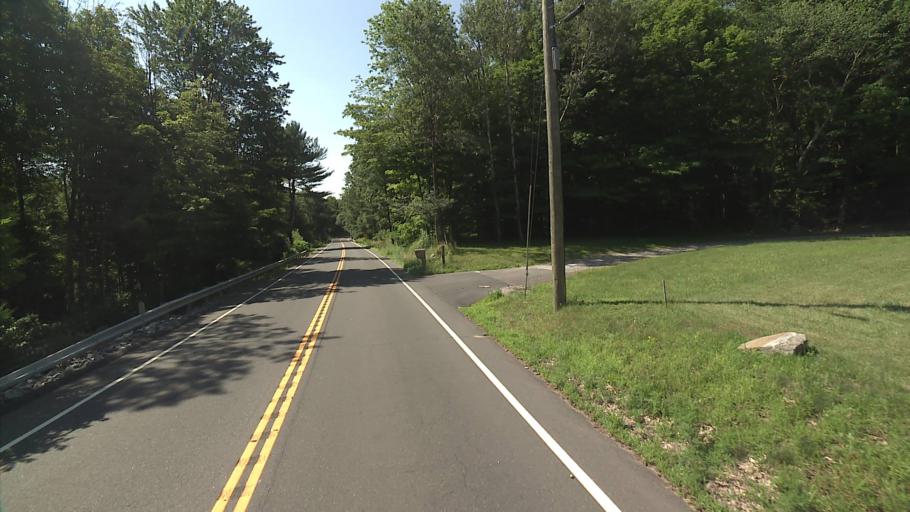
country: US
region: Connecticut
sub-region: Litchfield County
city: Terryville
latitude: 41.6961
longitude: -73.0059
